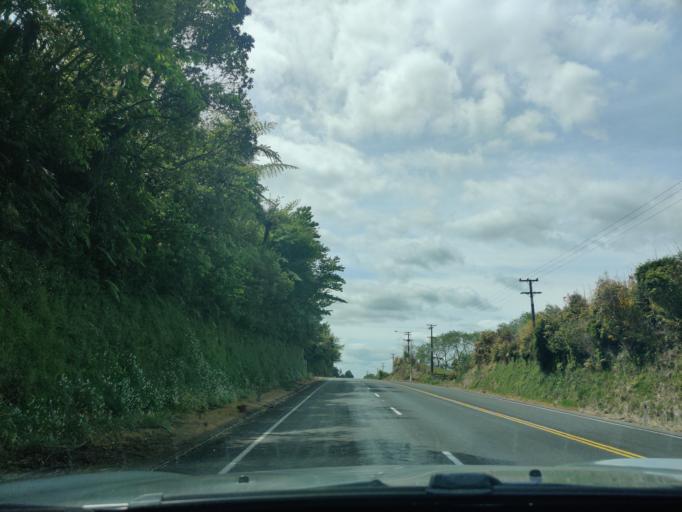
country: NZ
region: Taranaki
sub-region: New Plymouth District
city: New Plymouth
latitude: -39.1510
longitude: 174.1654
